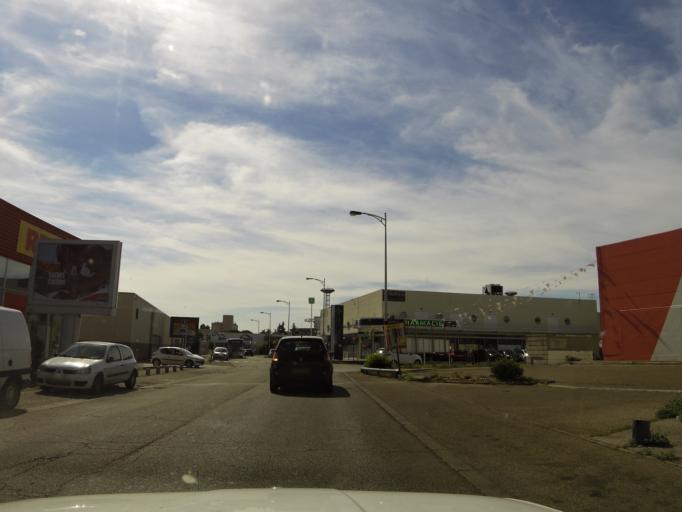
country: FR
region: Languedoc-Roussillon
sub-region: Departement du Gard
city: Nimes
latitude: 43.8166
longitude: 4.3505
